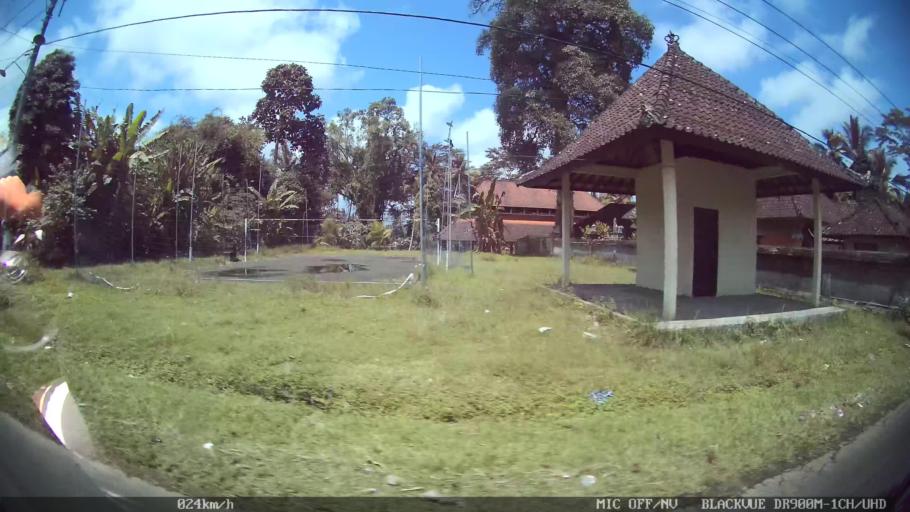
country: ID
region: Bali
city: Banjar Apuan Kaja
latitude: -8.5050
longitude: 115.3381
